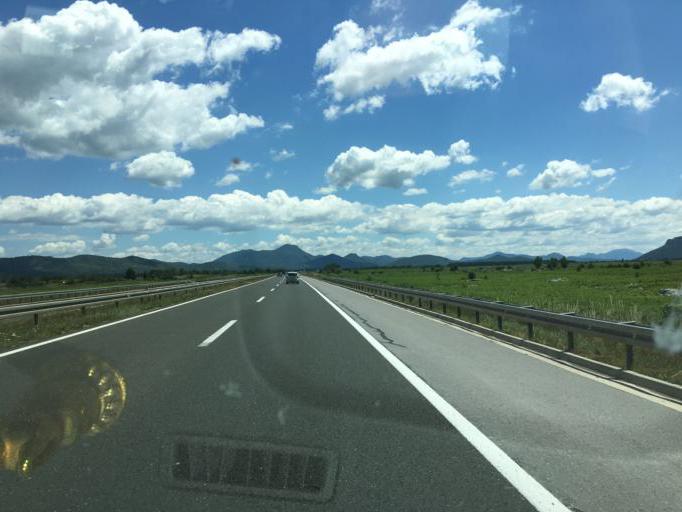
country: HR
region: Licko-Senjska
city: Gospic
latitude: 44.4798
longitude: 15.5634
